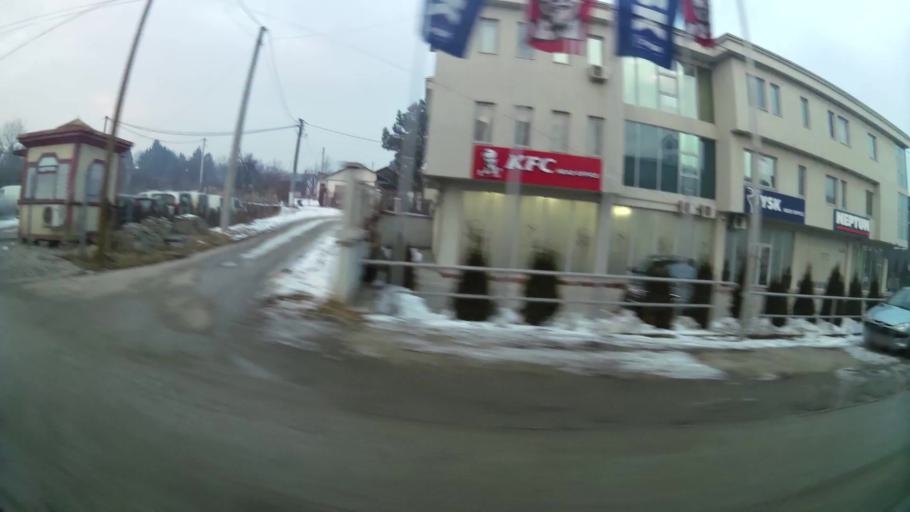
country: MK
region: Suto Orizari
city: Suto Orizare
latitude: 42.0278
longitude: 21.4094
